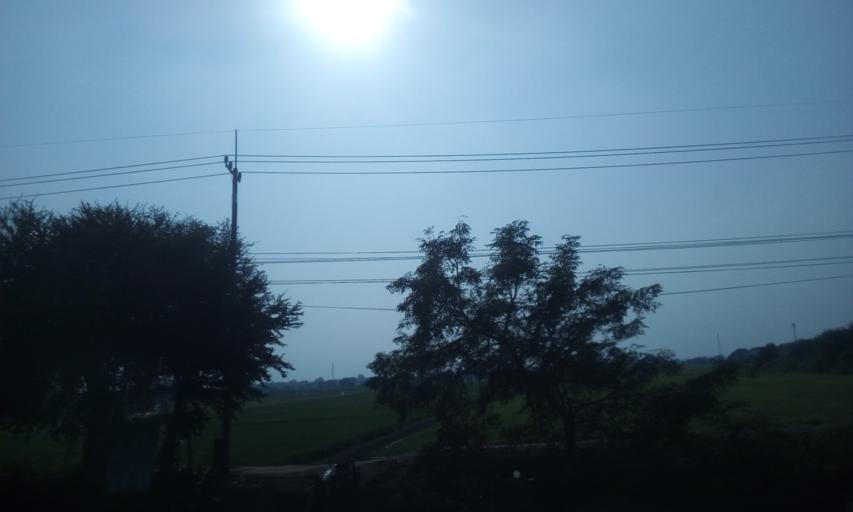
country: TH
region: Sing Buri
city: Phrom Buri
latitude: 14.7735
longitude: 100.4368
